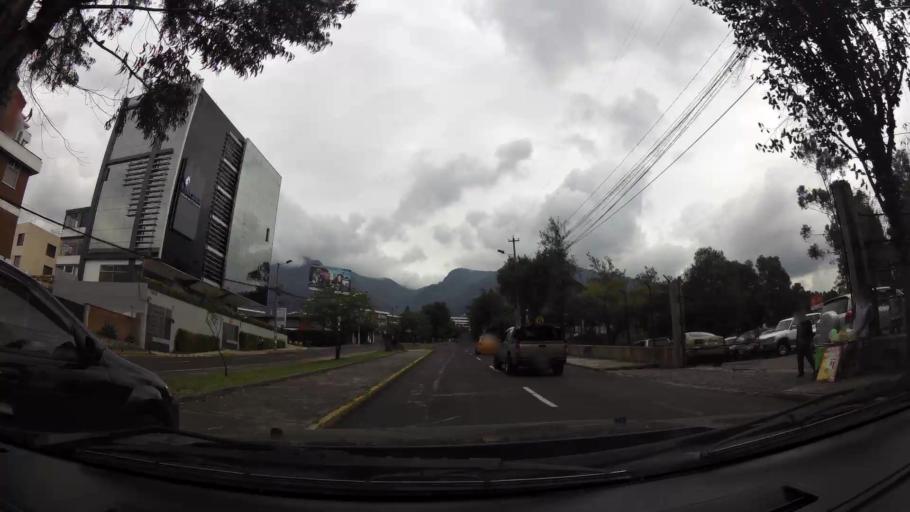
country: EC
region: Pichincha
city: Quito
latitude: -0.1852
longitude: -78.4984
